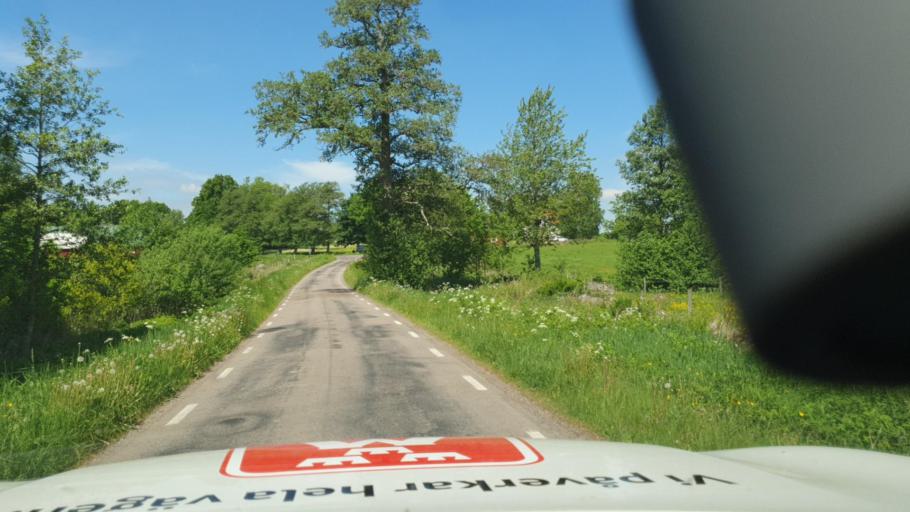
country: SE
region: Vaestra Goetaland
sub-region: Herrljunga Kommun
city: Herrljunga
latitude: 58.1446
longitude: 13.0709
